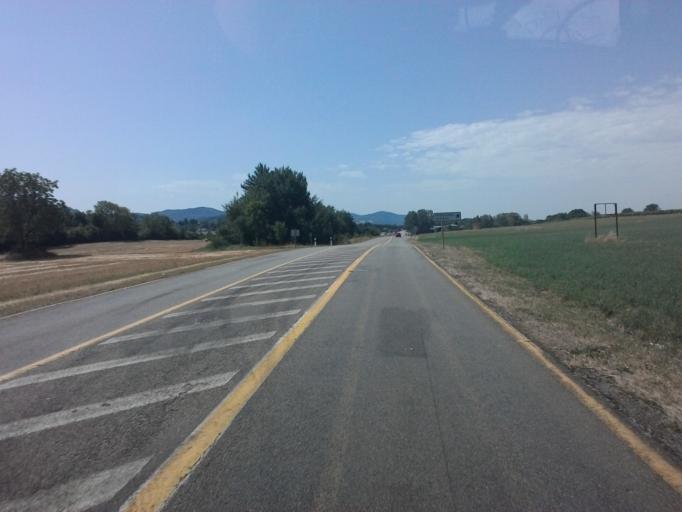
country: FR
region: Franche-Comte
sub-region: Departement du Jura
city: Montmorot
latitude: 46.6489
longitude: 5.5071
